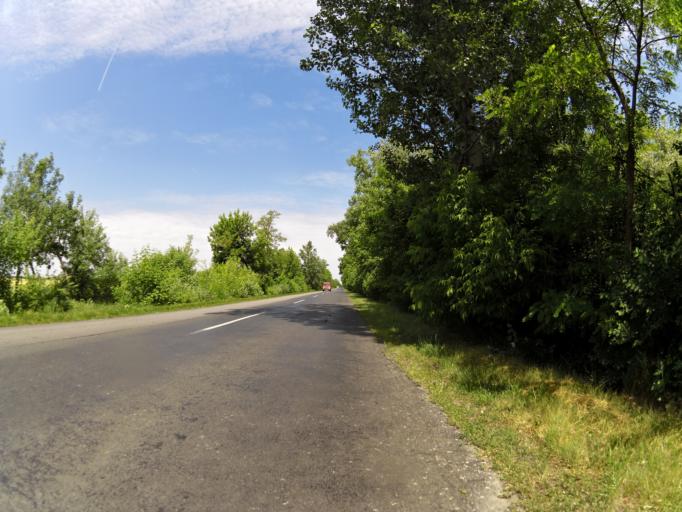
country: HU
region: Csongrad
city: Opusztaszer
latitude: 46.4357
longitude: 20.1076
